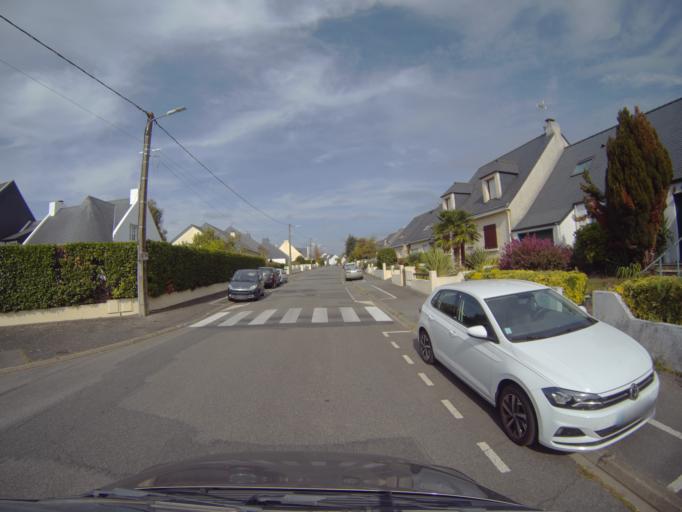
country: FR
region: Pays de la Loire
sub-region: Departement de la Loire-Atlantique
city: Saint-Herblain
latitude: 47.2133
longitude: -1.6437
